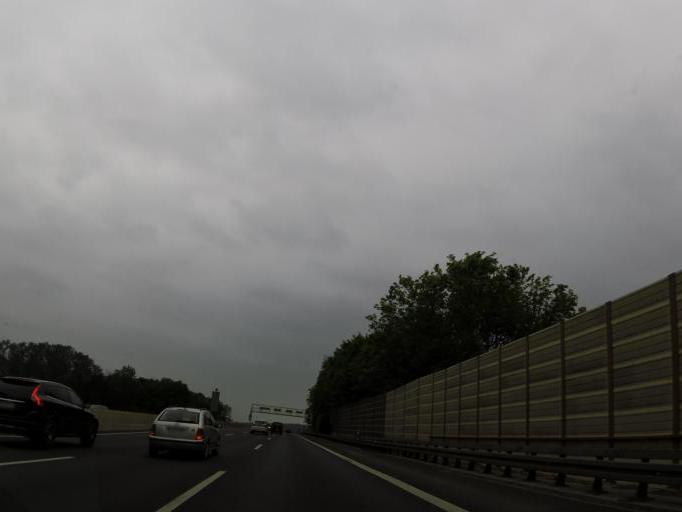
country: DE
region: Lower Saxony
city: Bovenden
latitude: 51.6129
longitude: 9.9079
